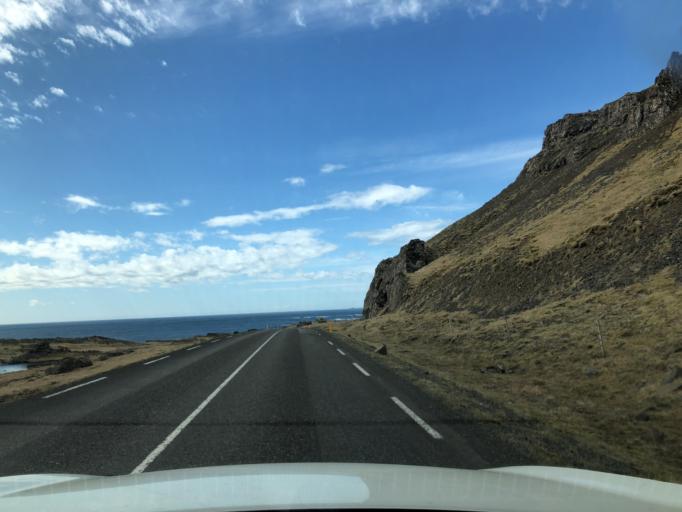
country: IS
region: East
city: Eskifjoerdur
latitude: 64.7324
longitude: -13.9900
